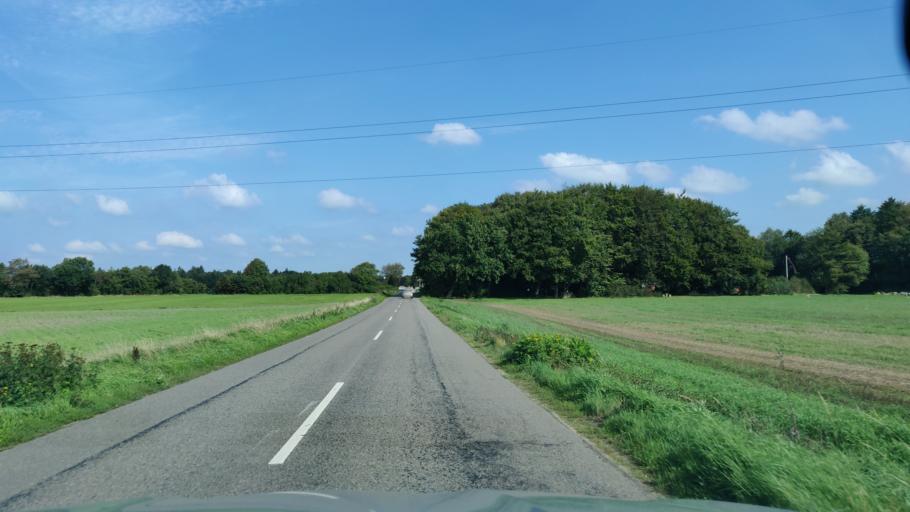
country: DK
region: Central Jutland
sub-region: Herning Kommune
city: Avlum
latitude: 56.2305
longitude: 8.8666
